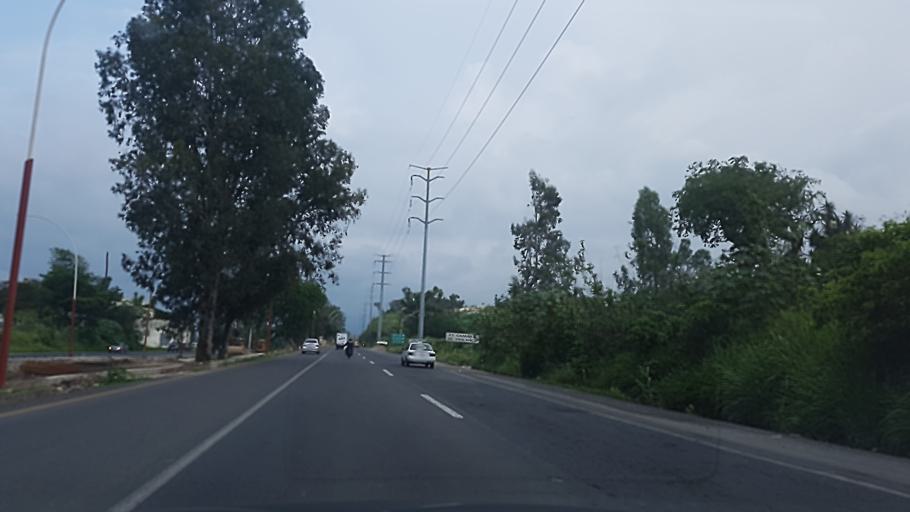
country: MX
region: Nayarit
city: Tepic
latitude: 21.4964
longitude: -104.9079
